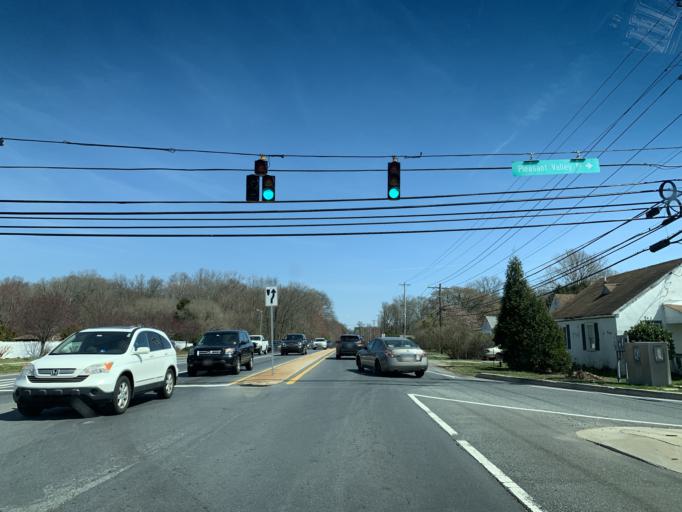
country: US
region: Delaware
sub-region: New Castle County
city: Glasgow
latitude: 39.6261
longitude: -75.7728
